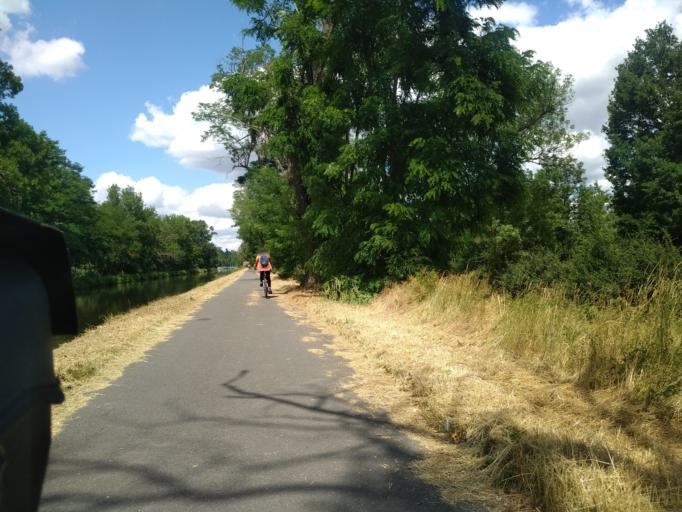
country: FR
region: Rhone-Alpes
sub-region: Departement de la Loire
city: Briennon
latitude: 46.1351
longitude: 4.0822
